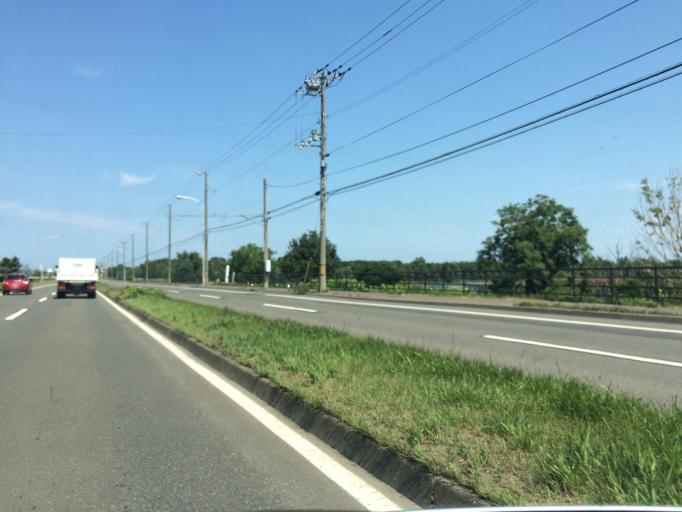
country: JP
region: Hokkaido
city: Sapporo
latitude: 43.1375
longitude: 141.2588
